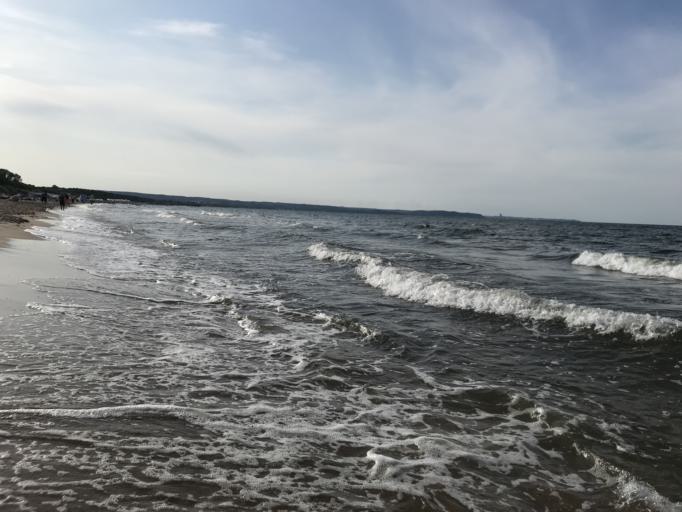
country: PL
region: Pomeranian Voivodeship
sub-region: Gdansk
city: Gdansk
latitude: 54.4097
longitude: 18.6380
